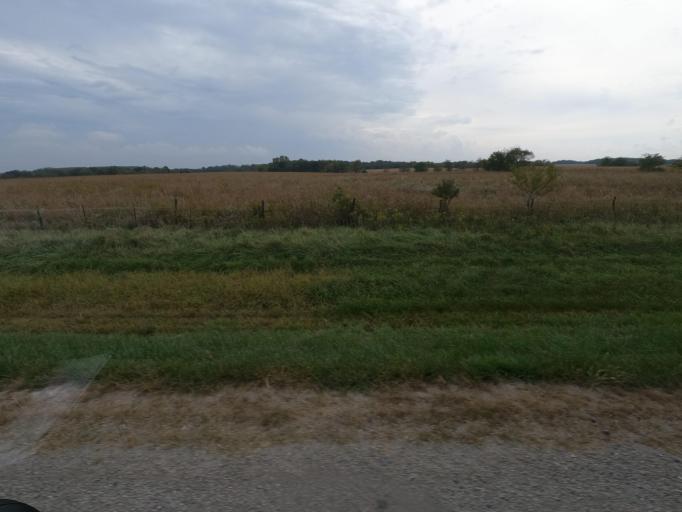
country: US
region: Iowa
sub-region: Van Buren County
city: Keosauqua
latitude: 40.8546
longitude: -92.0573
